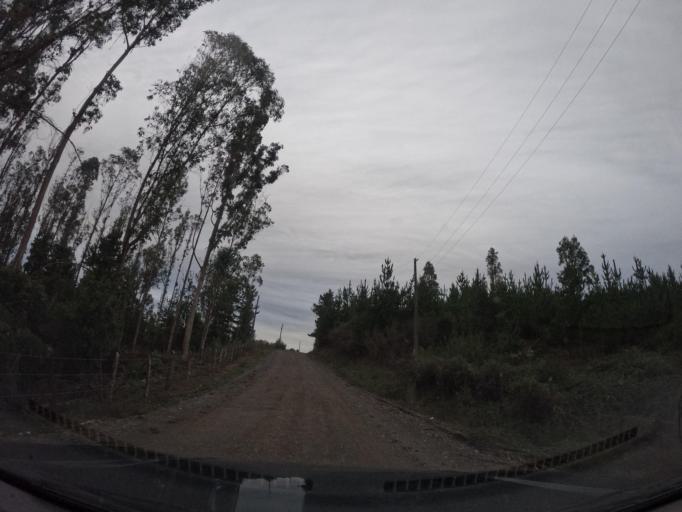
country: CL
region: Biobio
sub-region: Provincia de Concepcion
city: Chiguayante
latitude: -37.0146
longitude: -72.8612
